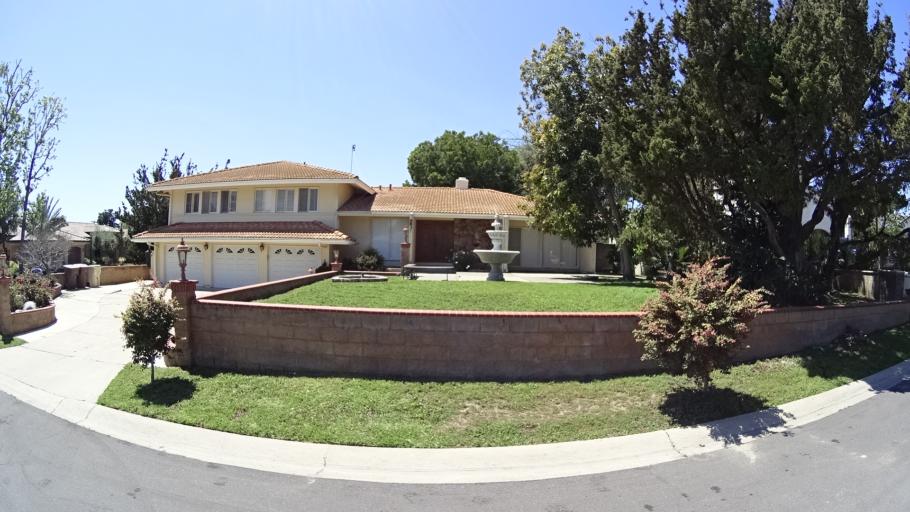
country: US
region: California
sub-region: Orange County
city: Villa Park
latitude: 33.8223
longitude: -117.8124
